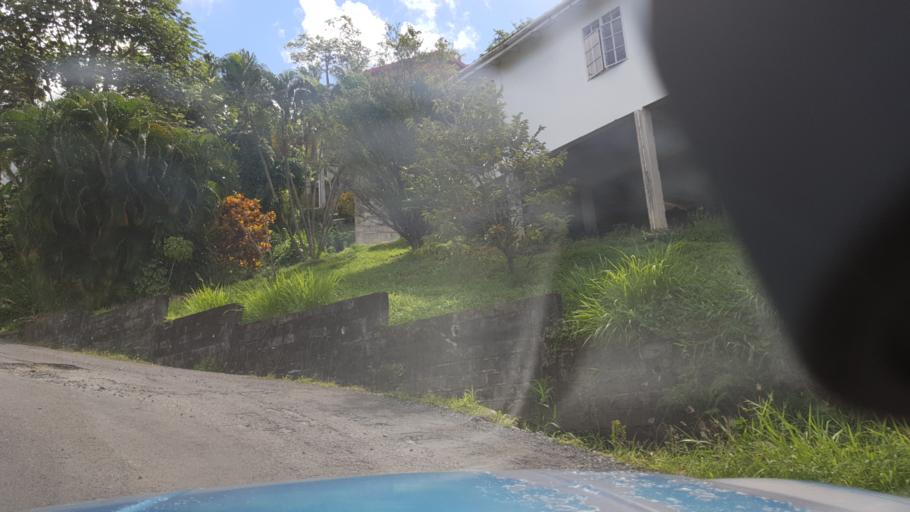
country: LC
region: Gros-Islet
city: Gros Islet
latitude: 14.0446
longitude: -60.9551
